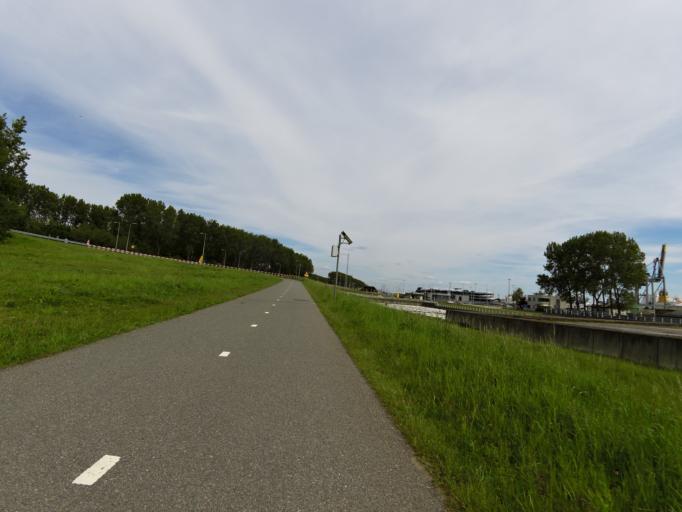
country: NL
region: South Holland
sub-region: Gemeente Maassluis
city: Maassluis
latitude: 51.9008
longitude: 4.2298
